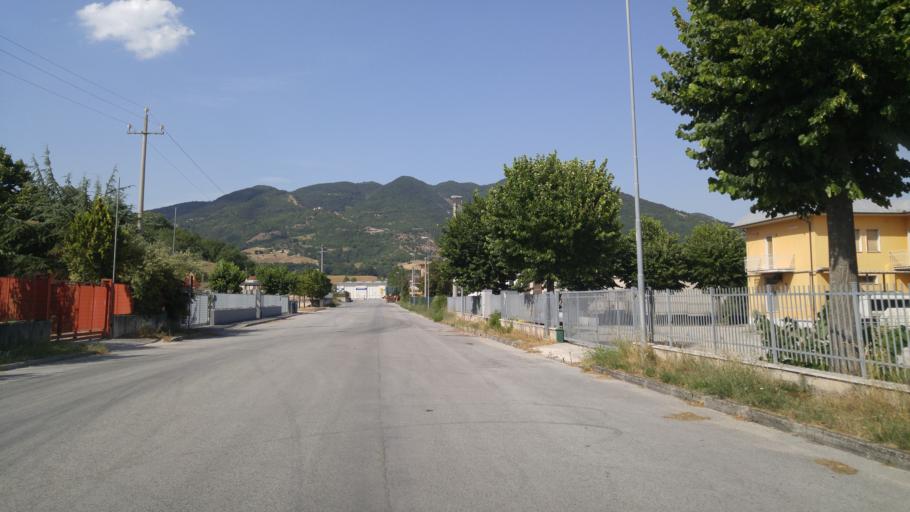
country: IT
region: The Marches
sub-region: Provincia di Pesaro e Urbino
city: Acqualagna
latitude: 43.6291
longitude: 12.6814
